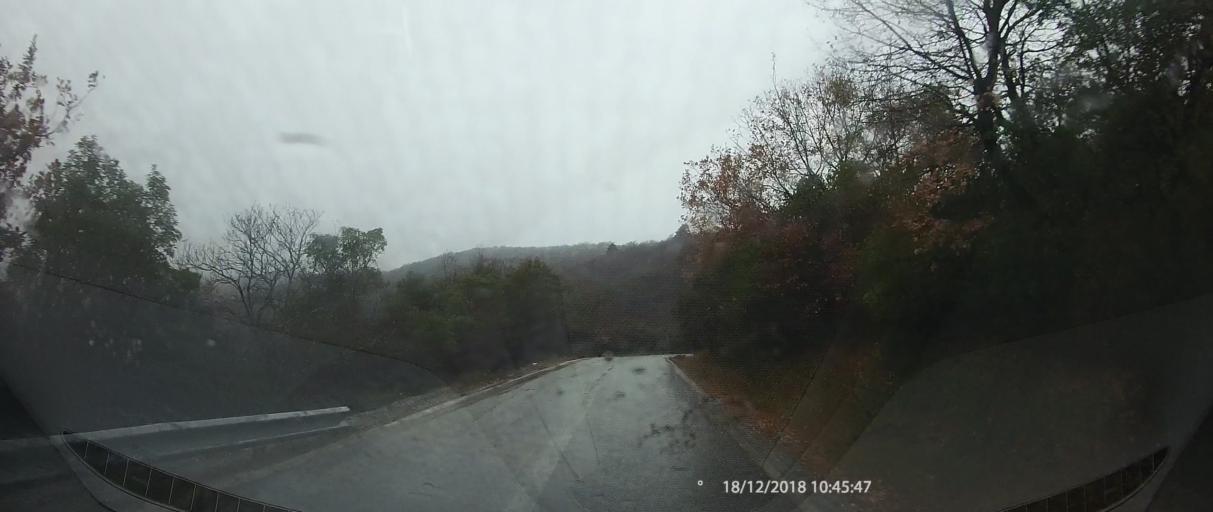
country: GR
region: Central Macedonia
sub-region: Nomos Pierias
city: Kato Milia
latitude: 40.1908
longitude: 22.3255
